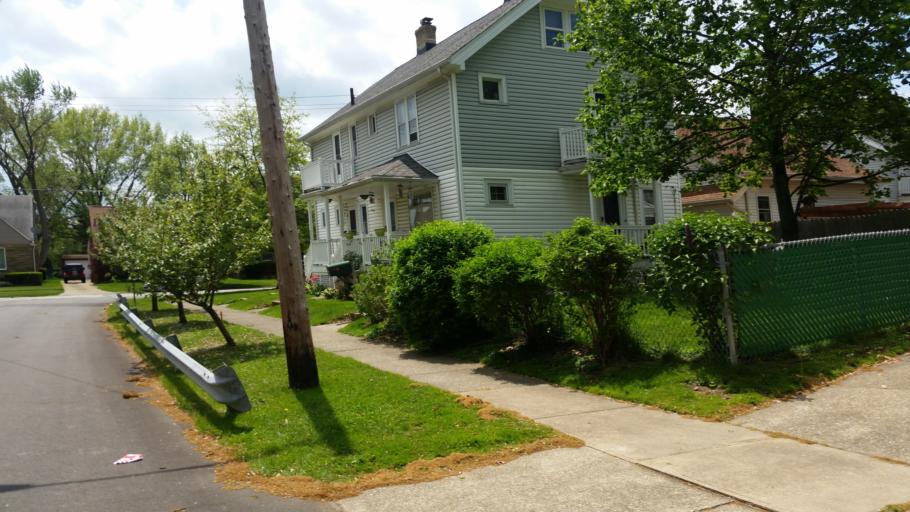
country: US
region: Ohio
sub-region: Cuyahoga County
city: Brooklyn Heights
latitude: 41.4271
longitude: -81.7010
